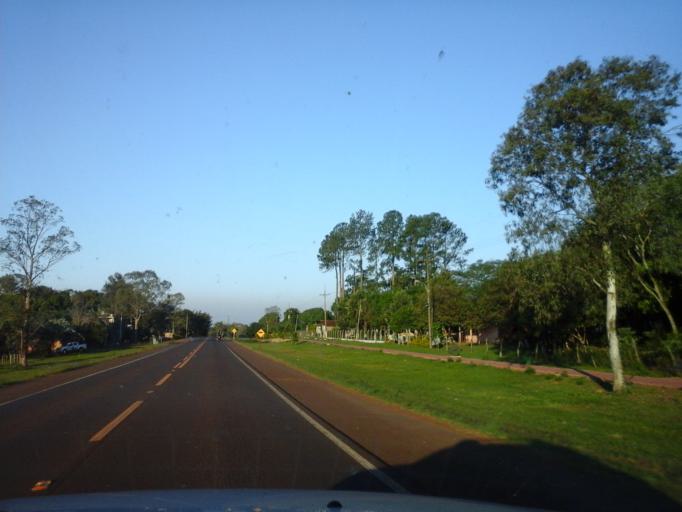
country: PY
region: Itapua
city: General Delgado
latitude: -27.0756
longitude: -56.5806
